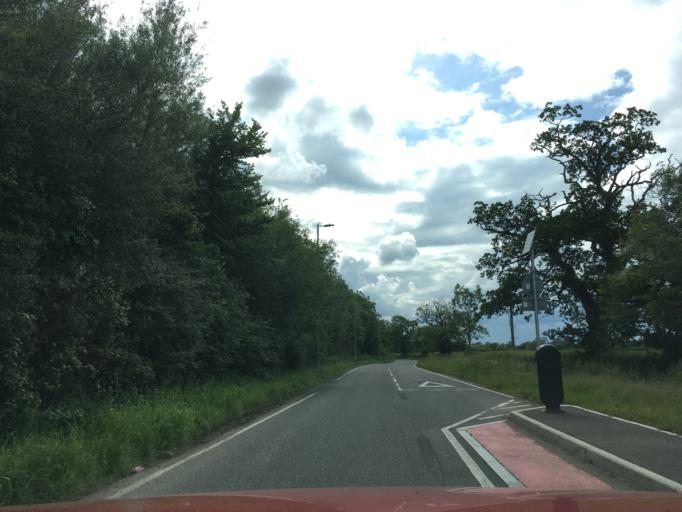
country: GB
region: England
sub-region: Wiltshire
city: Purton
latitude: 51.6050
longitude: -1.8330
